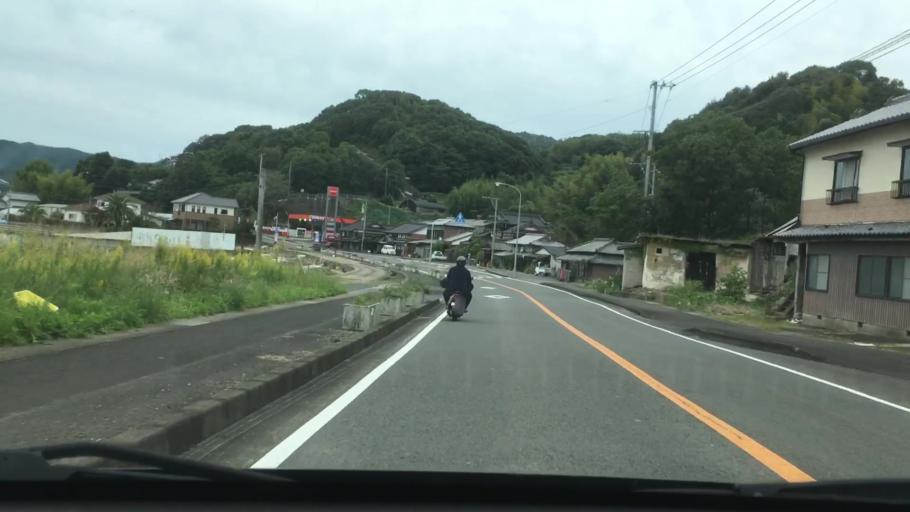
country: JP
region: Nagasaki
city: Sasebo
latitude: 33.0090
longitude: 129.7322
